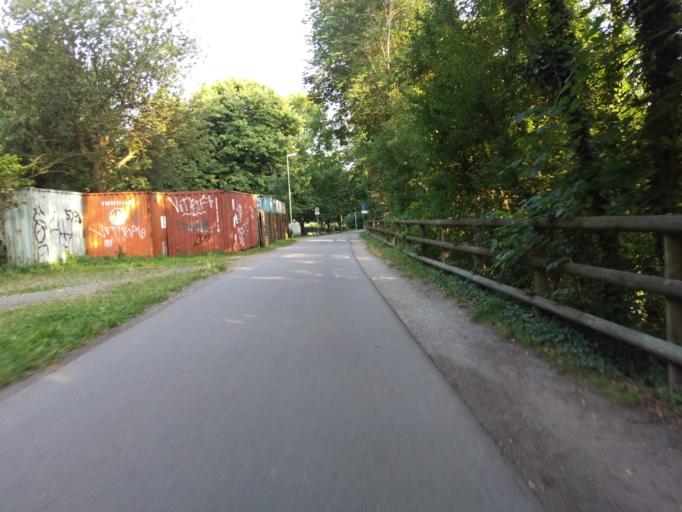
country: AT
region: Styria
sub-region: Graz Stadt
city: Goesting
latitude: 47.0909
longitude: 15.4220
